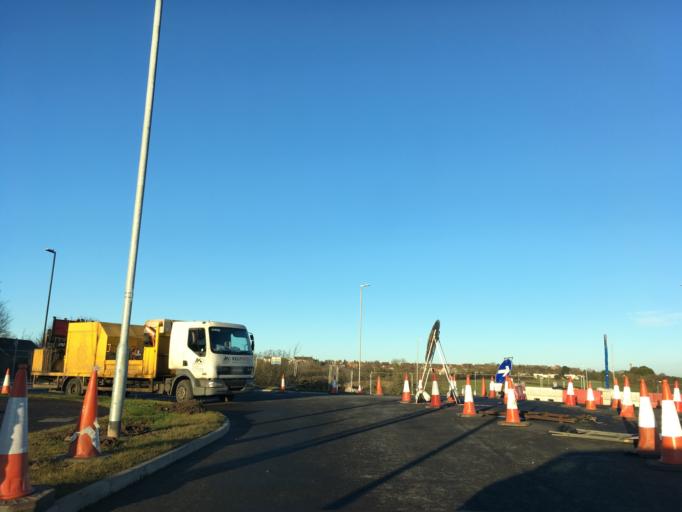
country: GB
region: England
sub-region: South Gloucestershire
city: Stoke Gifford
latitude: 51.5079
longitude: -2.5378
